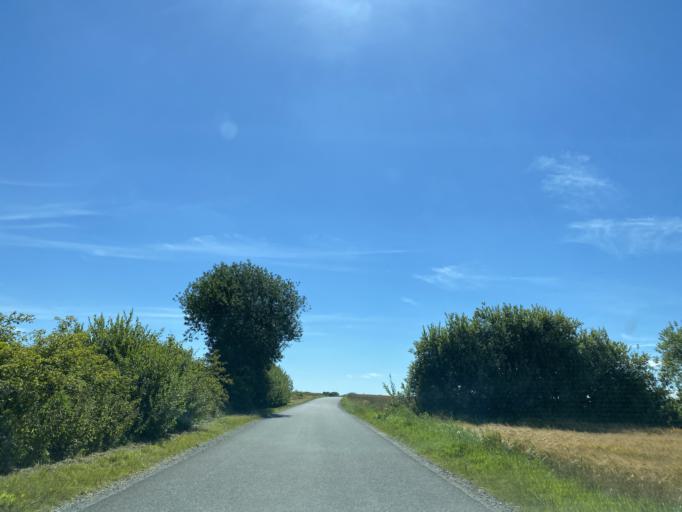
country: DK
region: South Denmark
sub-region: Vejle Kommune
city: Vejle
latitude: 55.6151
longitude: 9.5348
